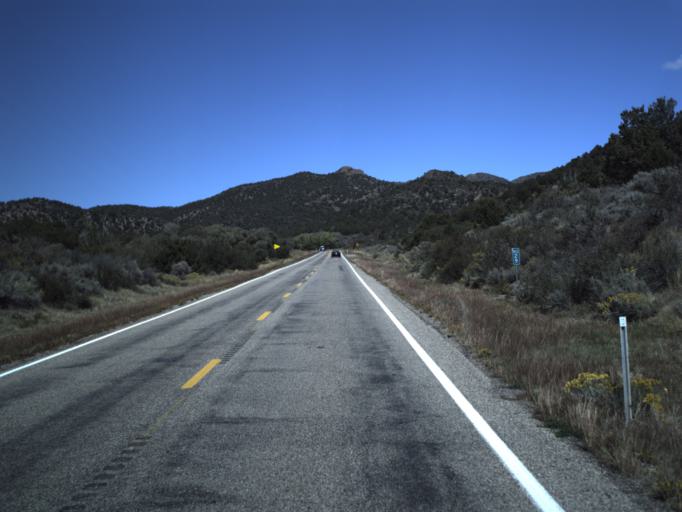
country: US
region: Utah
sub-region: Washington County
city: Enterprise
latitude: 37.4476
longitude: -113.6237
